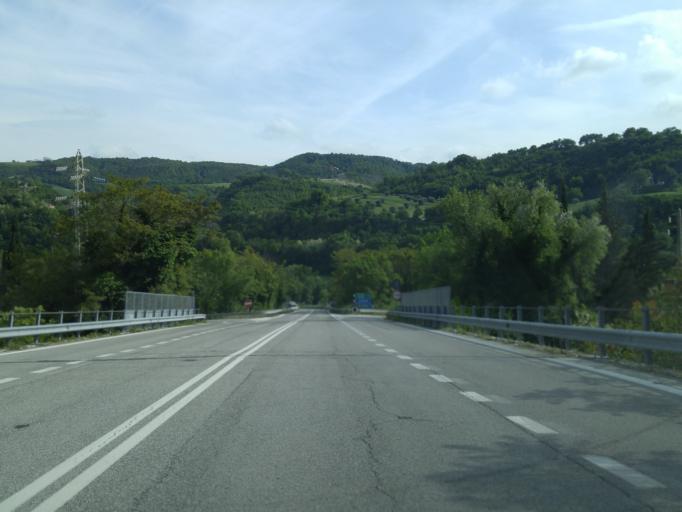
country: IT
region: The Marches
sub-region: Provincia di Pesaro e Urbino
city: Fossombrone
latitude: 43.6842
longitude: 12.7906
